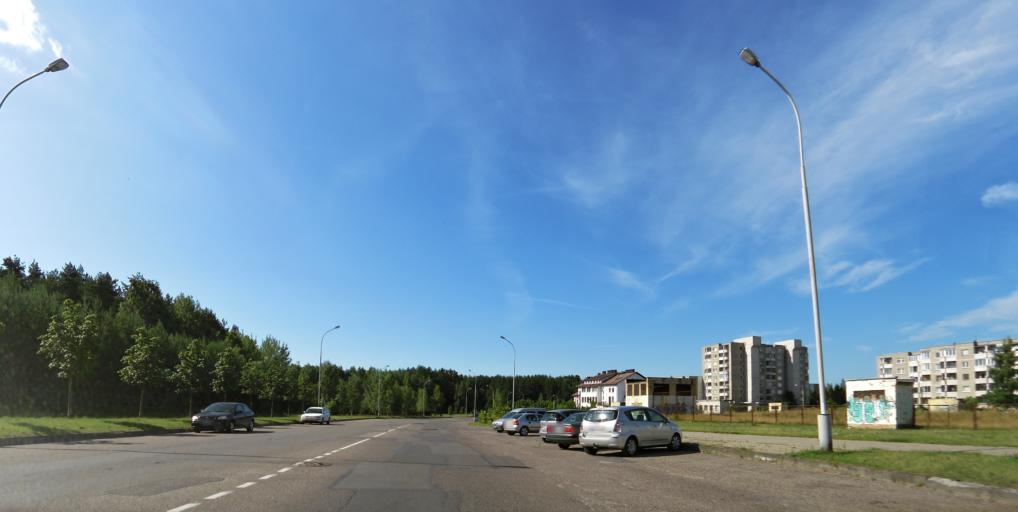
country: LT
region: Vilnius County
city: Pilaite
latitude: 54.7043
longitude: 25.1883
